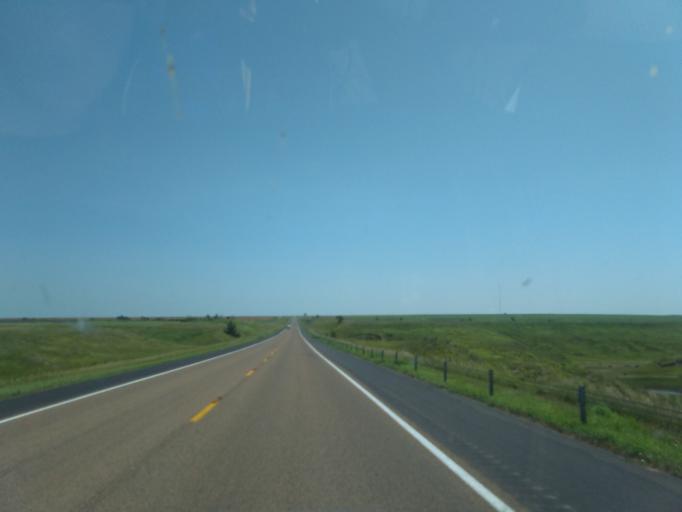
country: US
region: Nebraska
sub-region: Hitchcock County
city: Trenton
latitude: 40.2133
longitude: -100.9509
